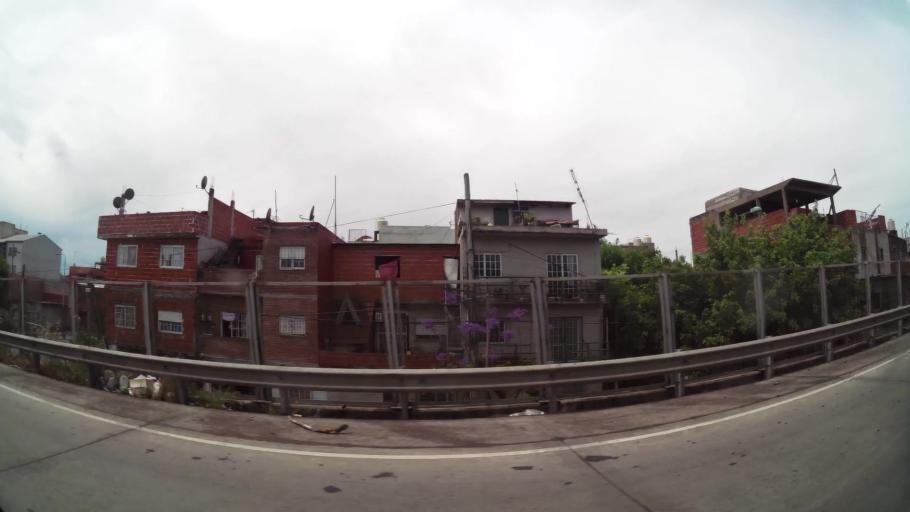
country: AR
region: Buenos Aires F.D.
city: Villa Lugano
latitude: -34.6615
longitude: -58.4545
